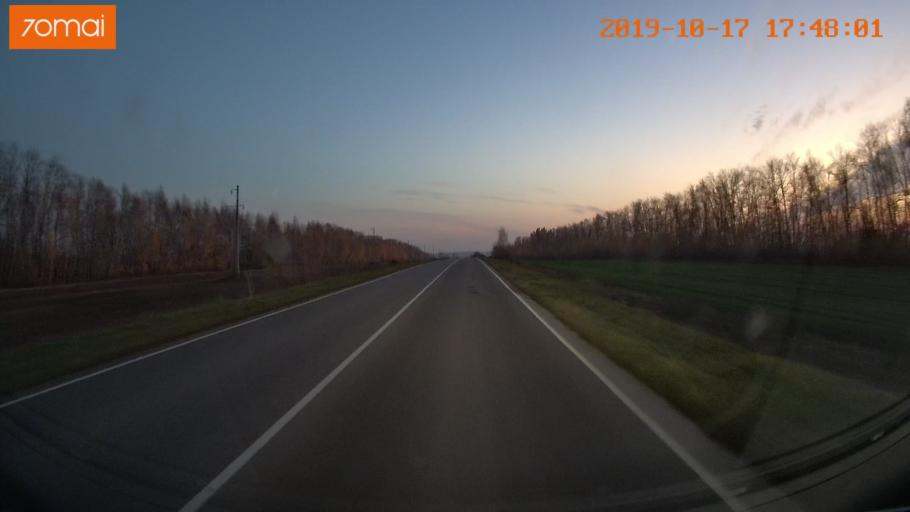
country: RU
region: Tula
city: Yepifan'
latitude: 53.6986
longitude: 38.6968
